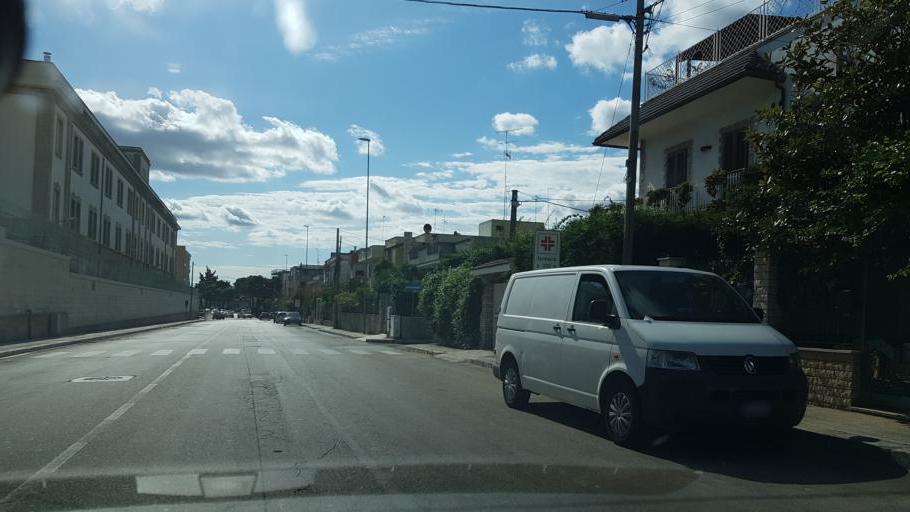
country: IT
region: Apulia
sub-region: Provincia di Lecce
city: Lecce
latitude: 40.3484
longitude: 18.1529
